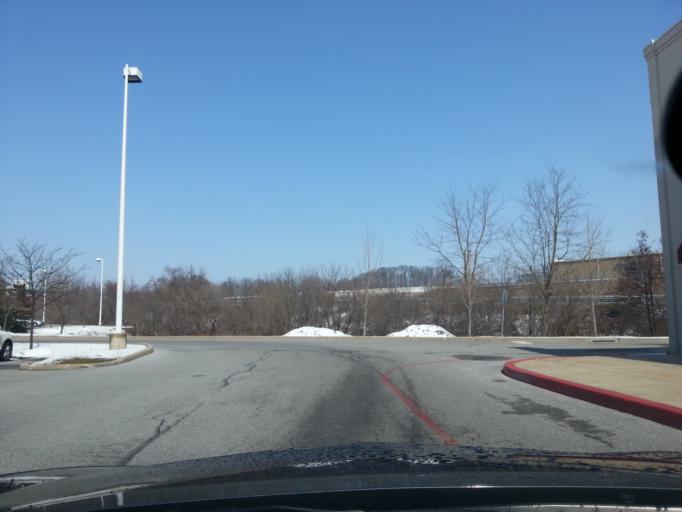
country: US
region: Pennsylvania
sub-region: York County
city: Shrewsbury
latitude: 39.7735
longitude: -76.6695
